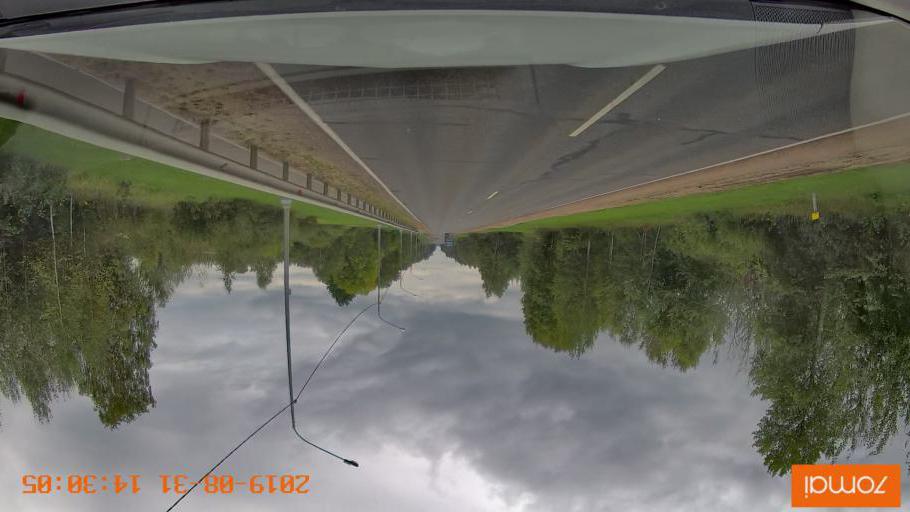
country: RU
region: Smolensk
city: Yekimovichi
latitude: 54.1296
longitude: 33.3444
